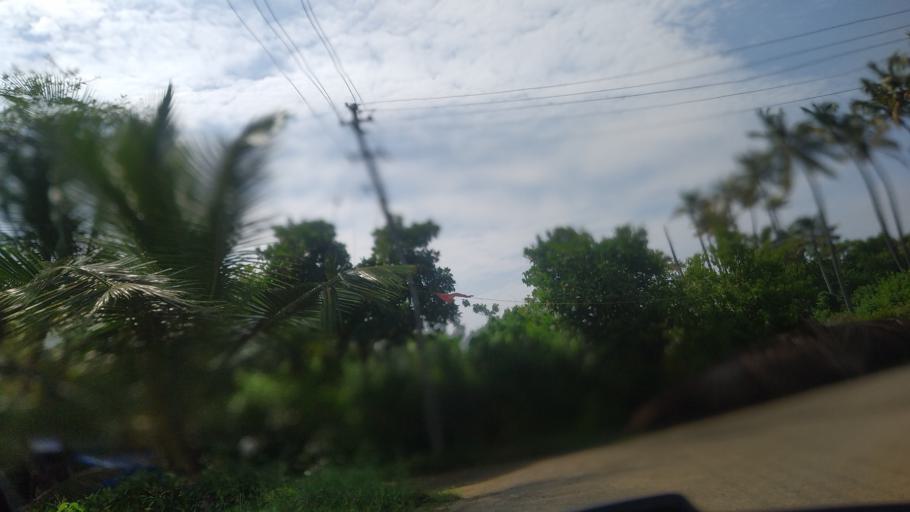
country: IN
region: Kerala
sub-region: Ernakulam
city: Elur
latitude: 10.0811
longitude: 76.1966
